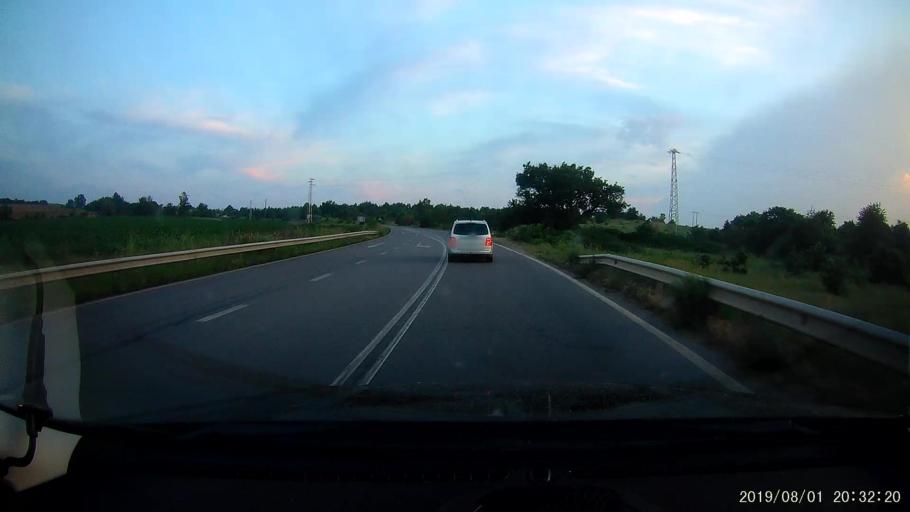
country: BG
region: Yambol
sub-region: Obshtina Elkhovo
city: Elkhovo
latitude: 42.1234
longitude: 26.5310
